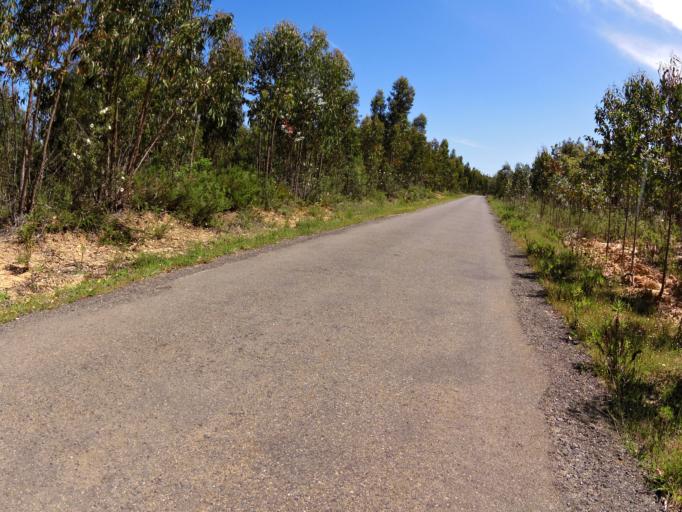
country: PT
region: Setubal
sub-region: Santiago do Cacem
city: Santiago do Cacem
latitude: 37.9466
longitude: -8.7263
